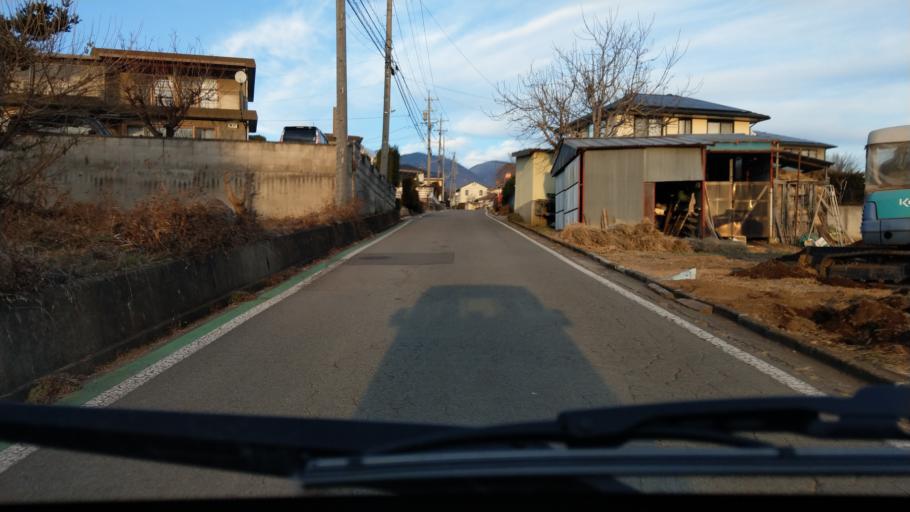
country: JP
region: Nagano
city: Komoro
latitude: 36.3447
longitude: 138.3893
